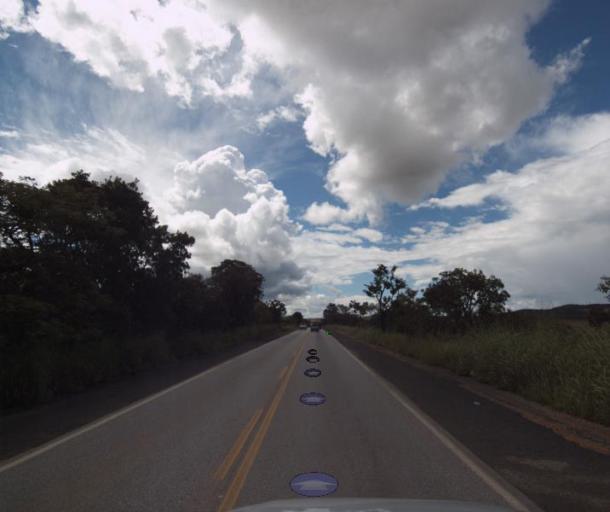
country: BR
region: Goias
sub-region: Uruacu
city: Uruacu
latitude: -14.0527
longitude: -49.0900
